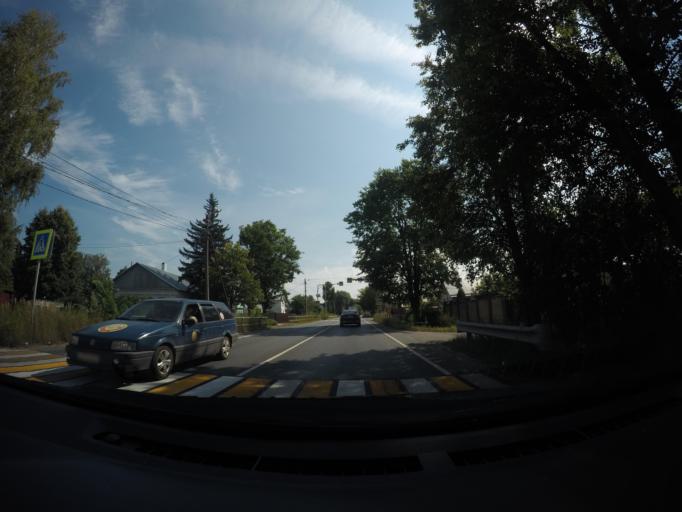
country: RU
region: Moskovskaya
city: Gzhel'
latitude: 55.6363
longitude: 38.3184
